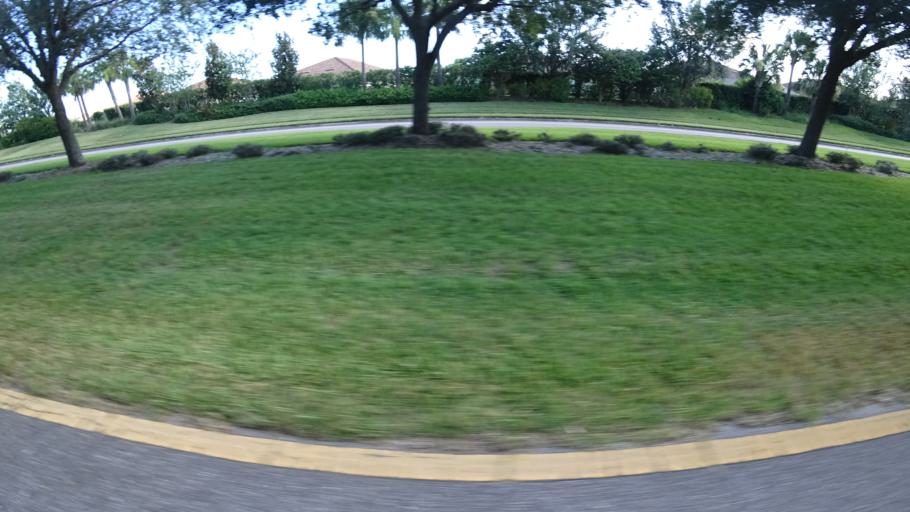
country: US
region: Florida
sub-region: Manatee County
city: Ellenton
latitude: 27.5061
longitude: -82.4788
